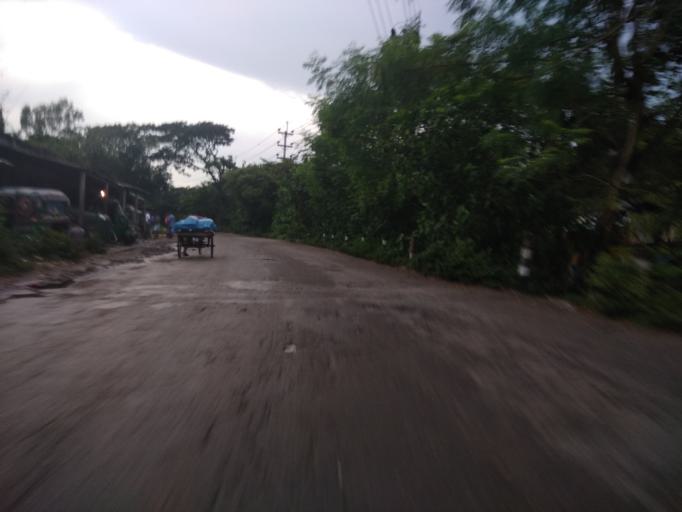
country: BD
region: Dhaka
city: Azimpur
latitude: 23.6714
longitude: 90.2922
